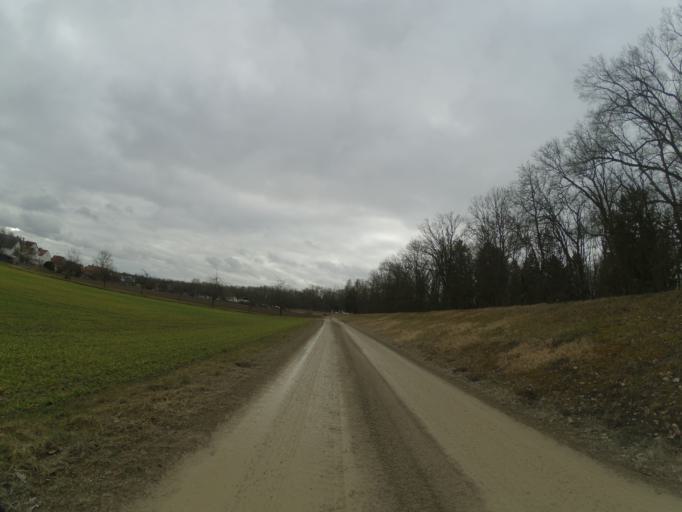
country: DE
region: Bavaria
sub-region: Swabia
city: Senden
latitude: 48.3019
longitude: 10.0481
